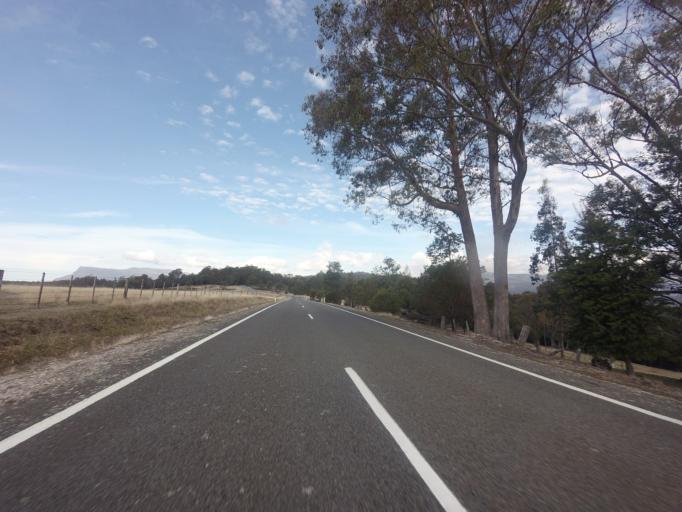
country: AU
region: Tasmania
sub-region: Meander Valley
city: Deloraine
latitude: -41.6627
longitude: 146.7245
